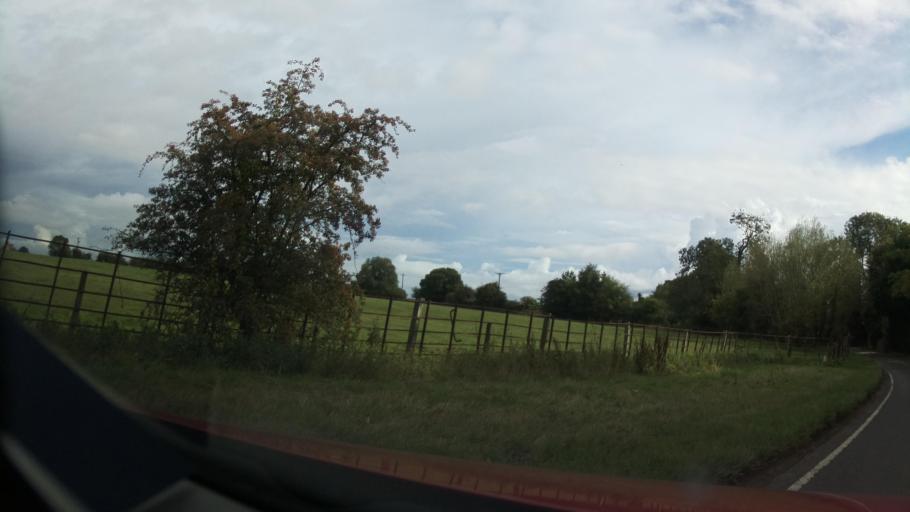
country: GB
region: England
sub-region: Telford and Wrekin
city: Madeley
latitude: 52.6284
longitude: -2.4141
